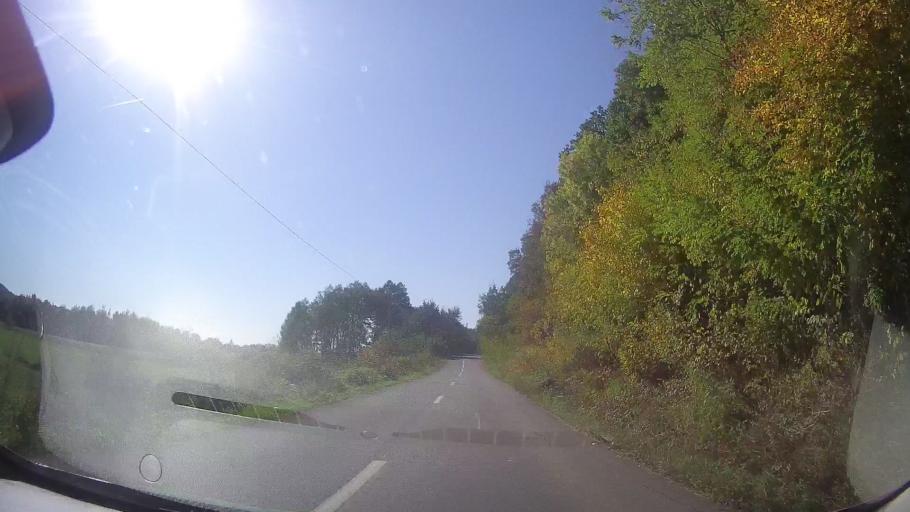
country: RO
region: Timis
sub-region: Comuna Ohaba Lunga
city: Ohaba Lunga
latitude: 45.8875
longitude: 21.9681
